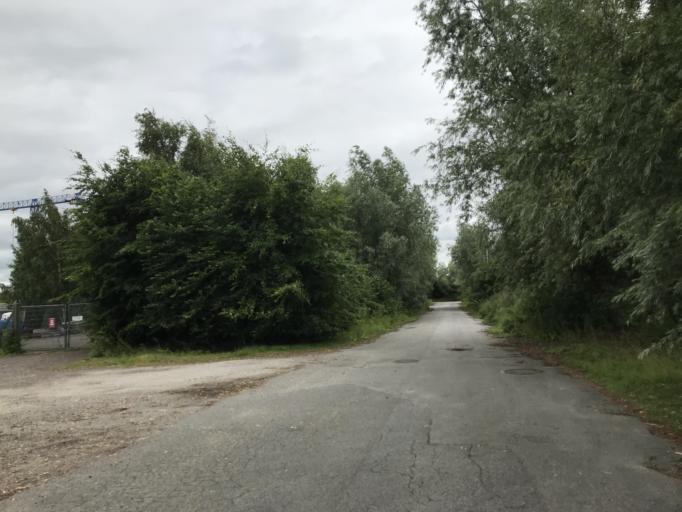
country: SE
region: Skane
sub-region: Burlovs Kommun
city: Arloev
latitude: 55.6207
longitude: 13.0872
